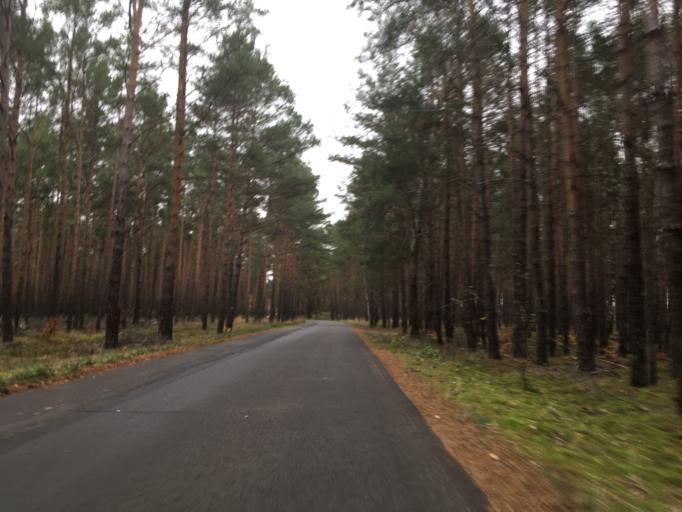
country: DE
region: Brandenburg
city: Mullrose
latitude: 52.2634
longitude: 14.4770
